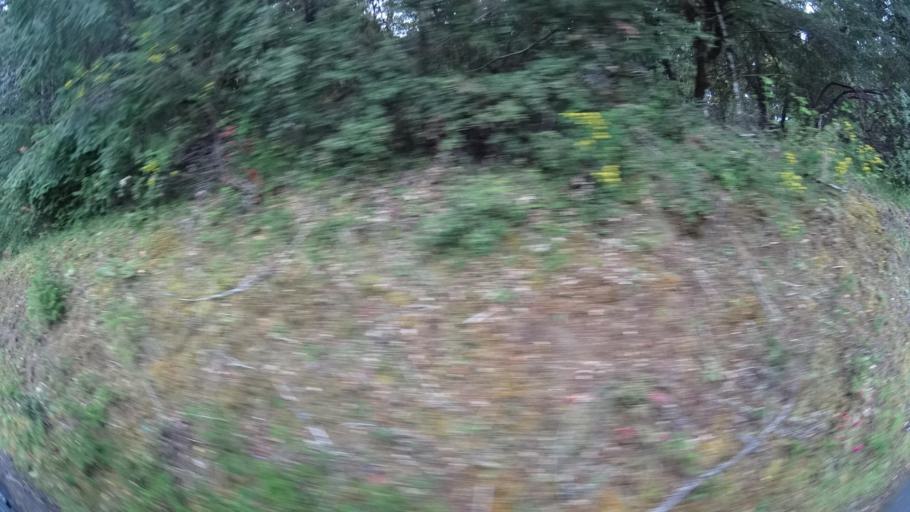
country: US
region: California
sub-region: Humboldt County
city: Redway
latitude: 40.2742
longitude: -123.7820
